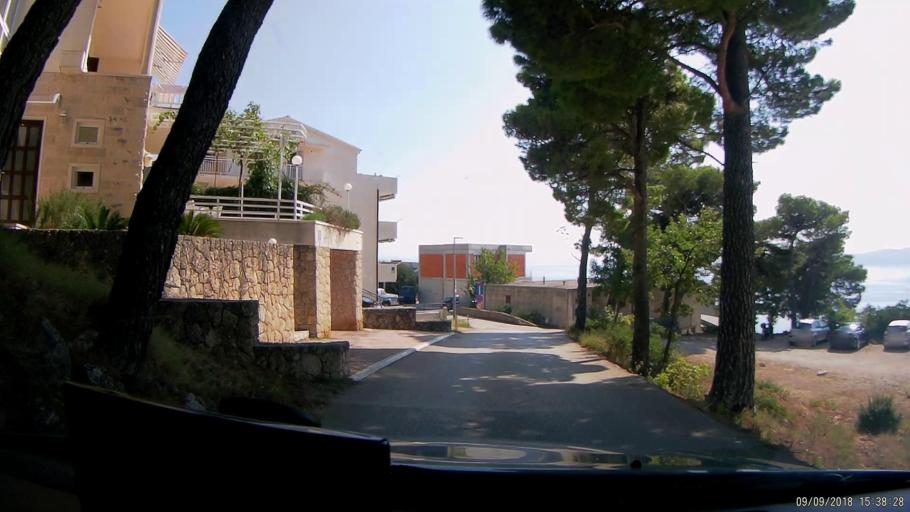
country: HR
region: Splitsko-Dalmatinska
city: Donja Brela
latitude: 43.3702
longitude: 16.9313
